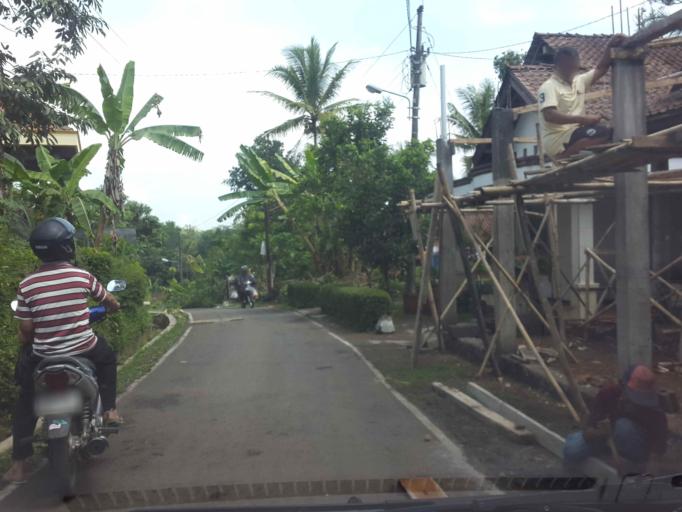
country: ID
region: Central Java
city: Salatiga
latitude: -7.3270
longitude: 110.5213
